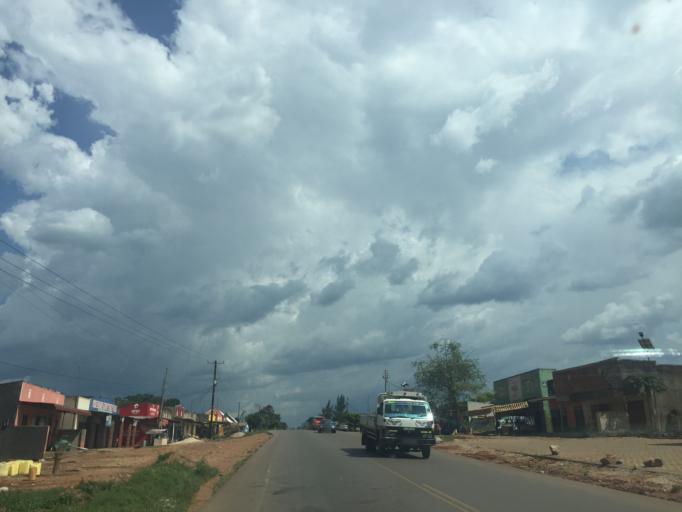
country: UG
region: Central Region
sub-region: Luwero District
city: Wobulenzi
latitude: 0.7347
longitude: 32.5238
